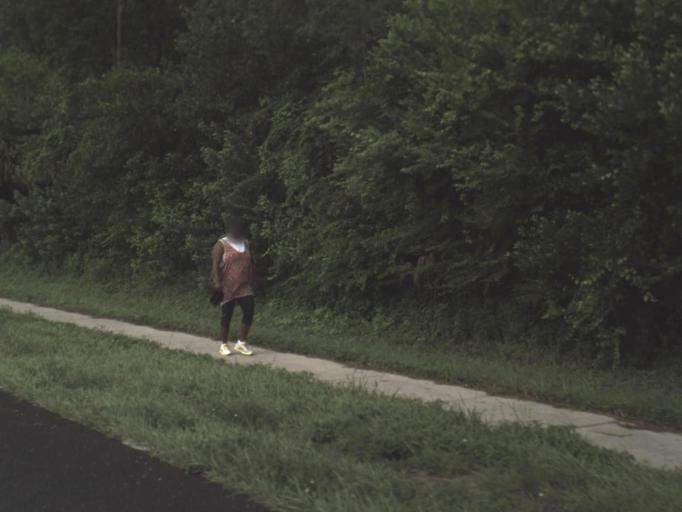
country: US
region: Florida
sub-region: Hillsborough County
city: East Lake-Orient Park
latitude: 27.9771
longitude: -82.4018
